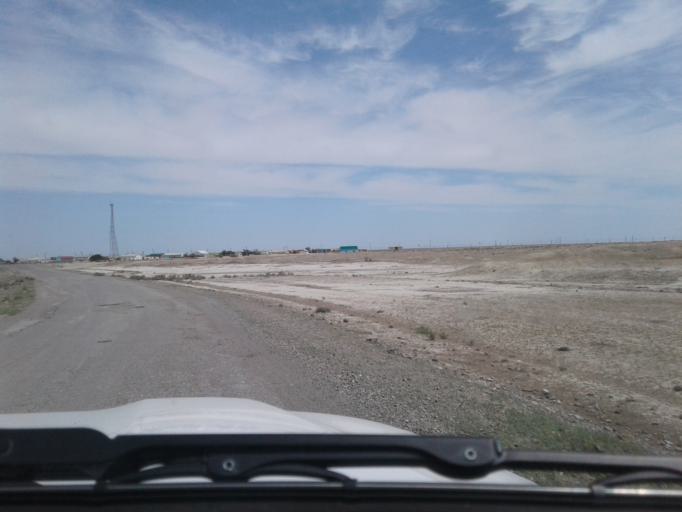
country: TM
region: Balkan
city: Gazanjyk
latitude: 39.2046
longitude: 55.7100
